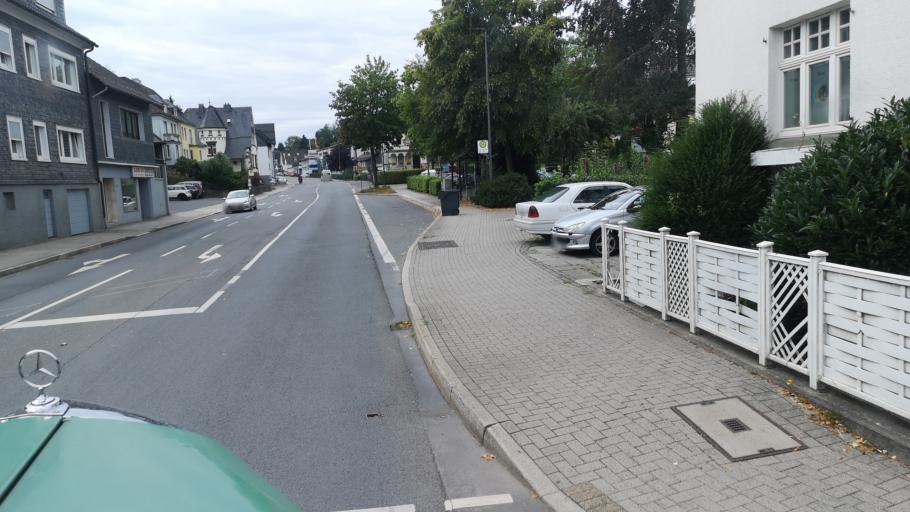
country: DE
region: North Rhine-Westphalia
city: Wipperfurth
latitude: 51.1151
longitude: 7.3903
